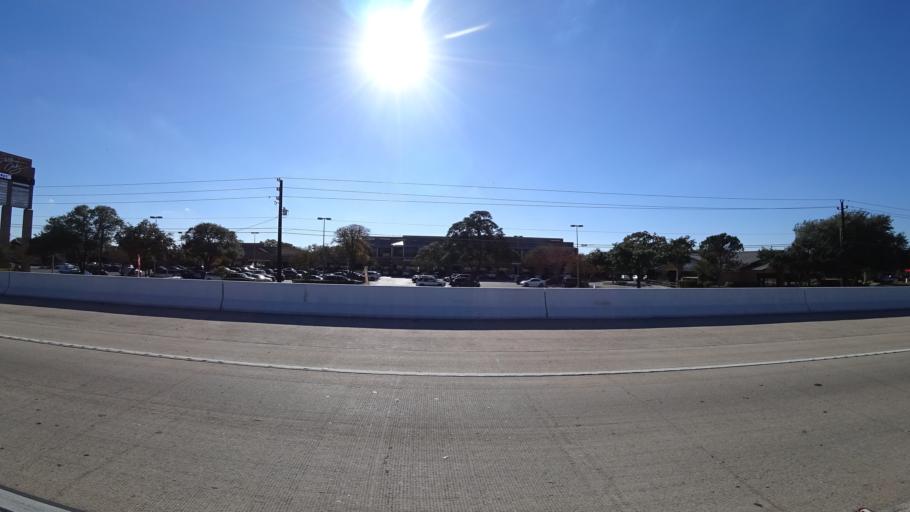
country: US
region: Texas
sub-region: Williamson County
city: Jollyville
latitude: 30.4452
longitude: -97.7884
